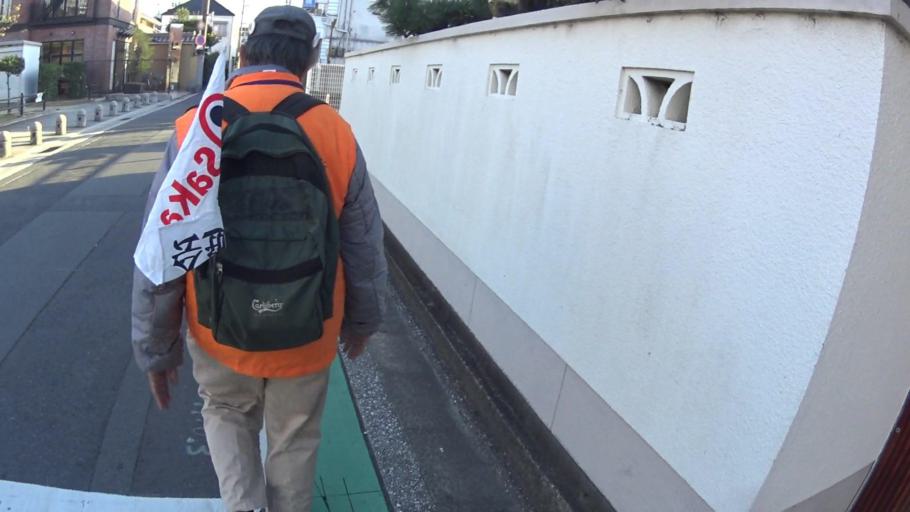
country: JP
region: Osaka
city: Kashihara
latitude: 34.5760
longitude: 135.5940
